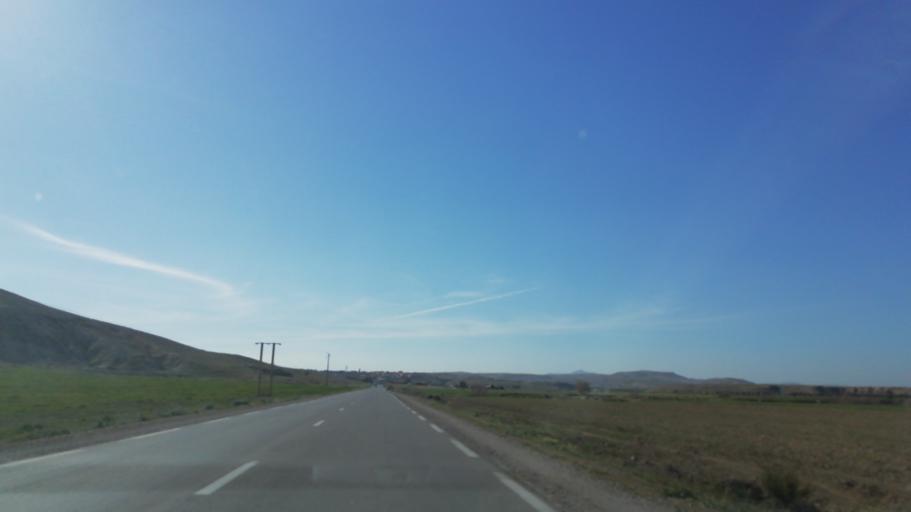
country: DZ
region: Mascara
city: Oued el Abtal
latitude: 35.4555
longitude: 0.7366
